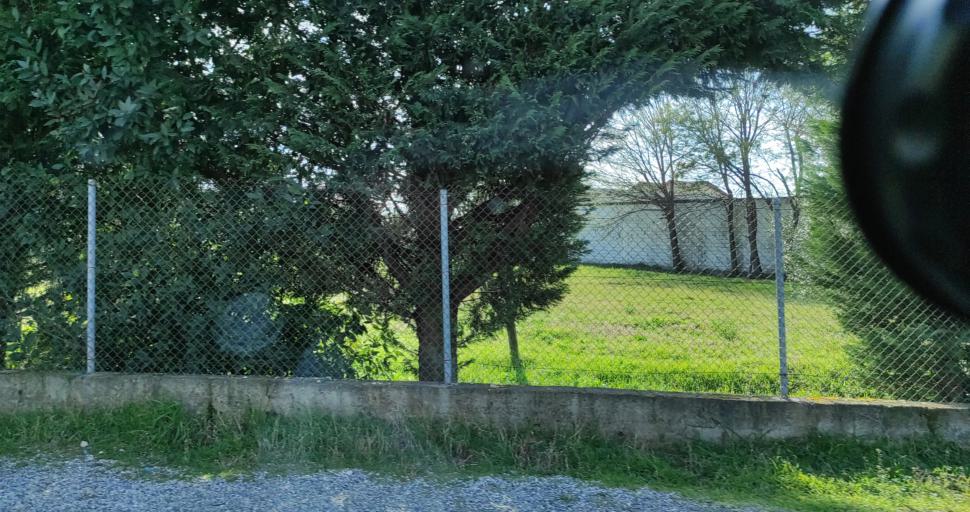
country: AL
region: Lezhe
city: Lezhe
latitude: 41.7789
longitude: 19.6329
